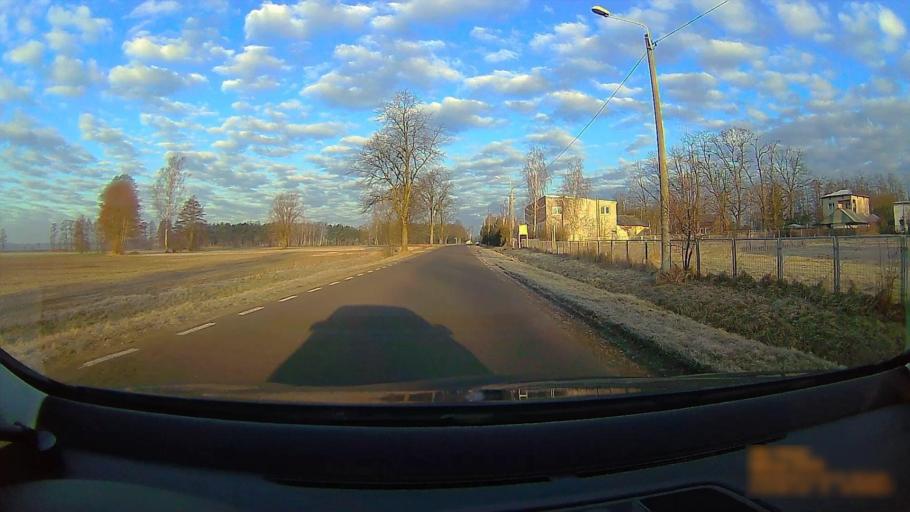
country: PL
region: Greater Poland Voivodeship
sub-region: Powiat koninski
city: Rzgow Pierwszy
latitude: 52.1005
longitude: 18.0995
